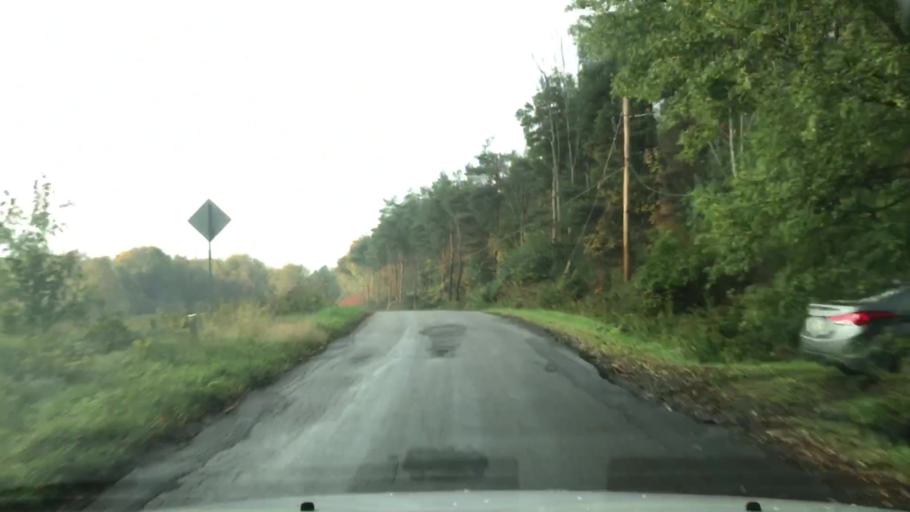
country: US
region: New York
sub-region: Cattaraugus County
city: Little Valley
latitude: 42.3059
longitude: -78.7163
